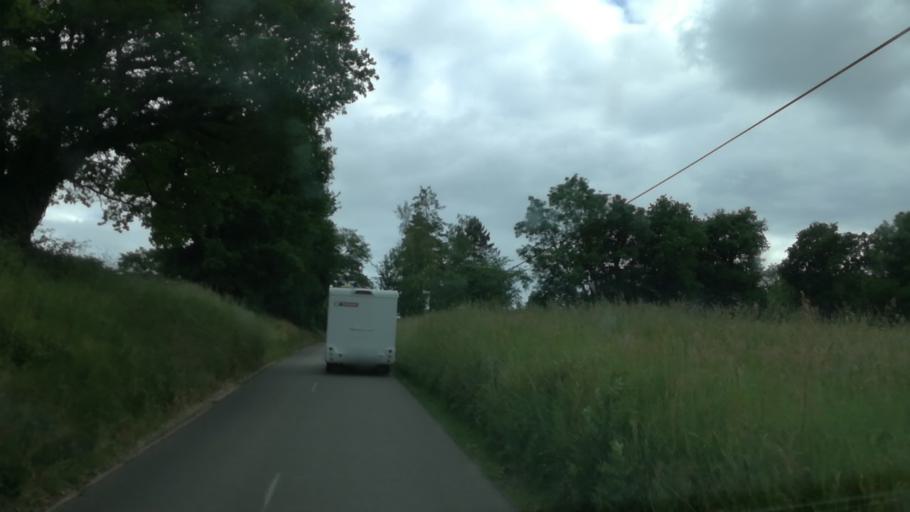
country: FR
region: Haute-Normandie
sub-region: Departement de l'Eure
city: Bourg-Achard
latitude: 49.3339
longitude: 0.8119
